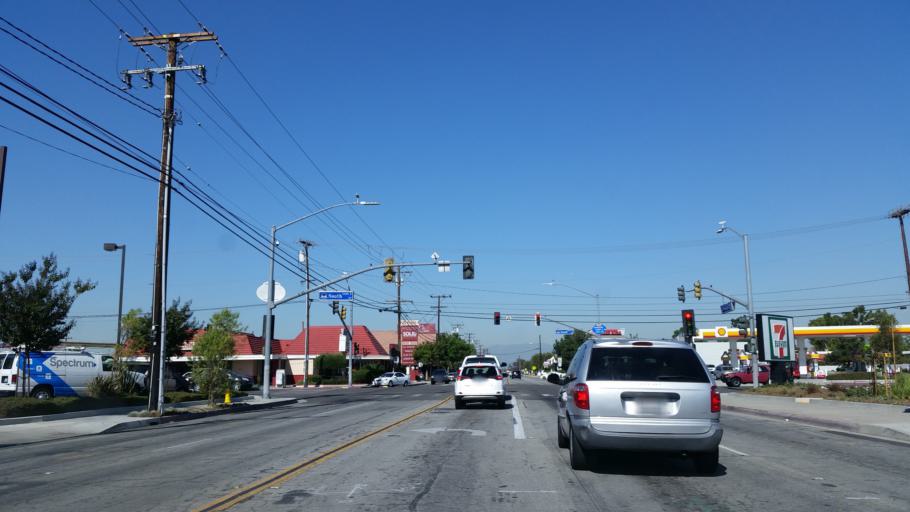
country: US
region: California
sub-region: Los Angeles County
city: Cerritos
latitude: 33.8580
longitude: -118.0723
